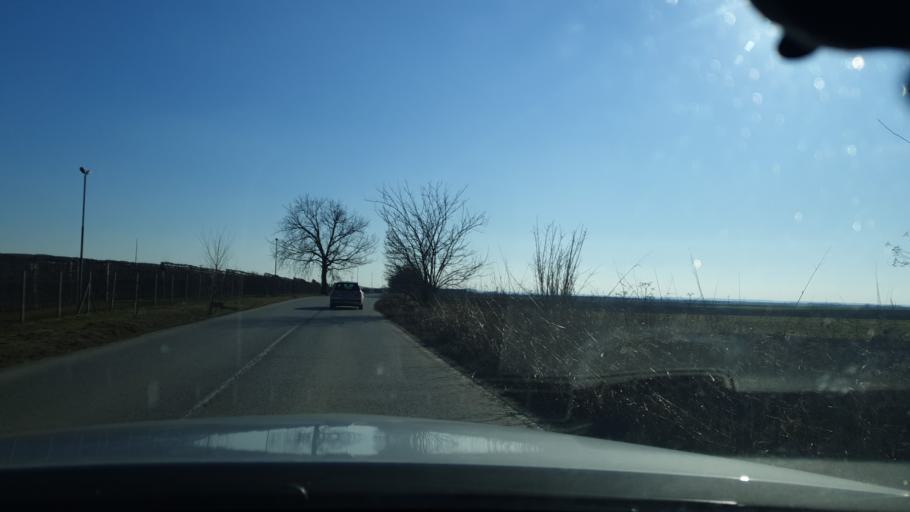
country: RS
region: Autonomna Pokrajina Vojvodina
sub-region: Sremski Okrug
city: Ruma
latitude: 45.0467
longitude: 19.8055
